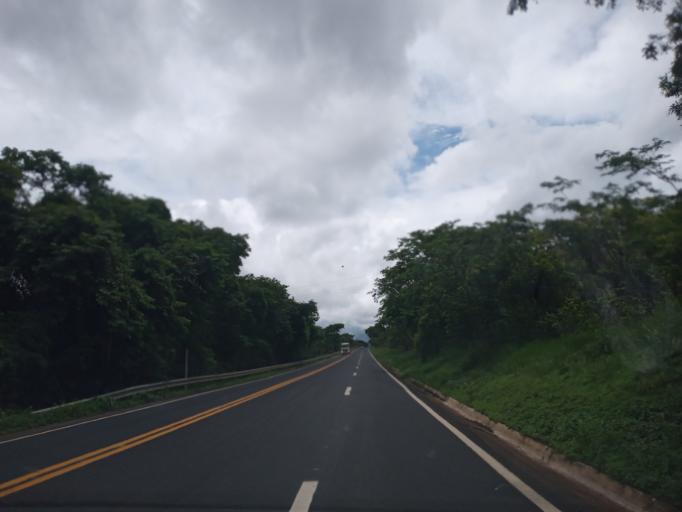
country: BR
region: Minas Gerais
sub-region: Uberaba
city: Uberaba
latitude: -19.2669
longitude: -47.6613
